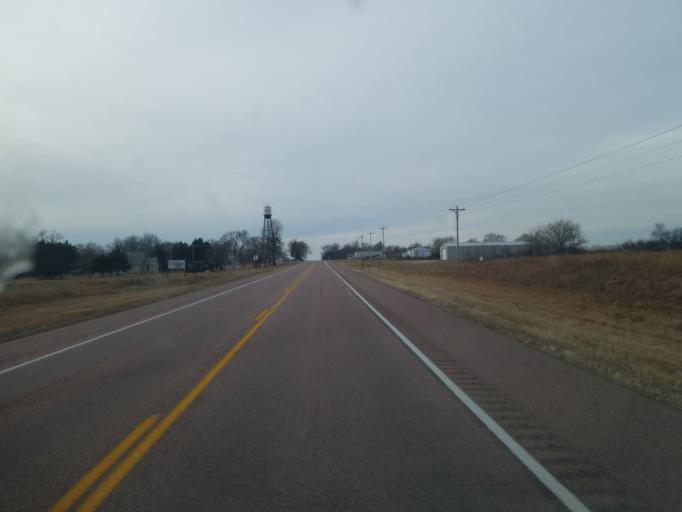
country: US
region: Nebraska
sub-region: Antelope County
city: Neligh
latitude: 42.3353
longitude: -98.1193
